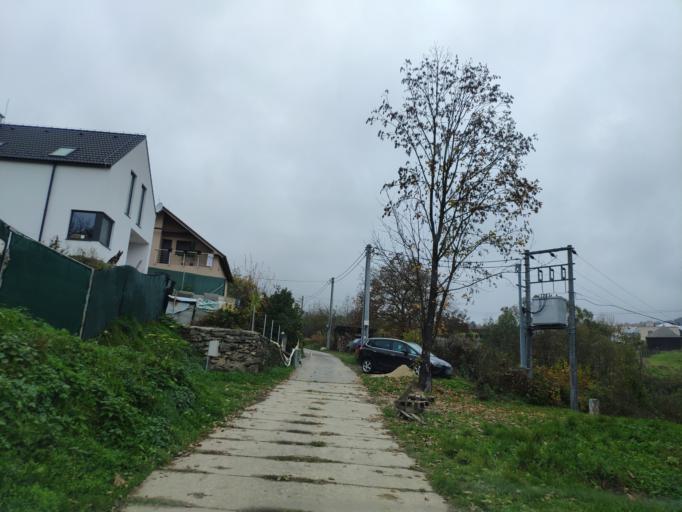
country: SK
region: Kosicky
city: Kosice
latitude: 48.7262
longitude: 21.1083
